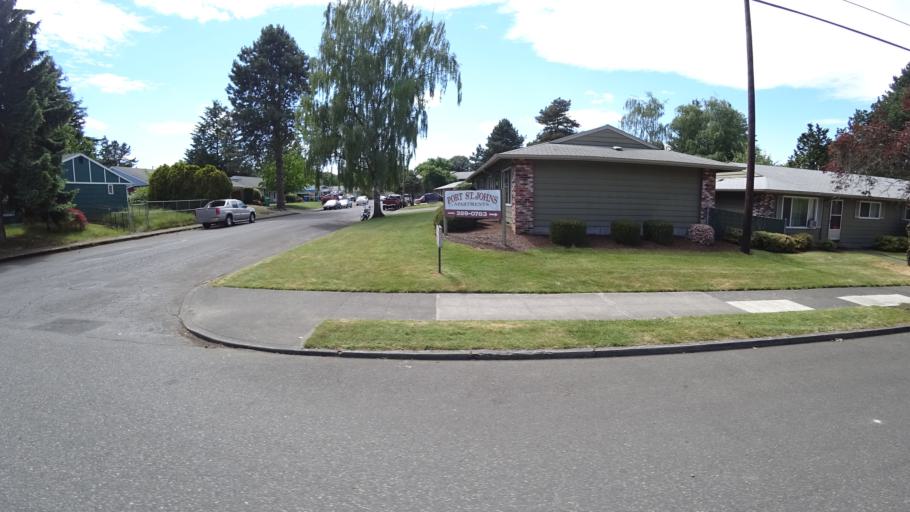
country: US
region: Washington
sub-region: Clark County
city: Vancouver
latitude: 45.5904
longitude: -122.7283
